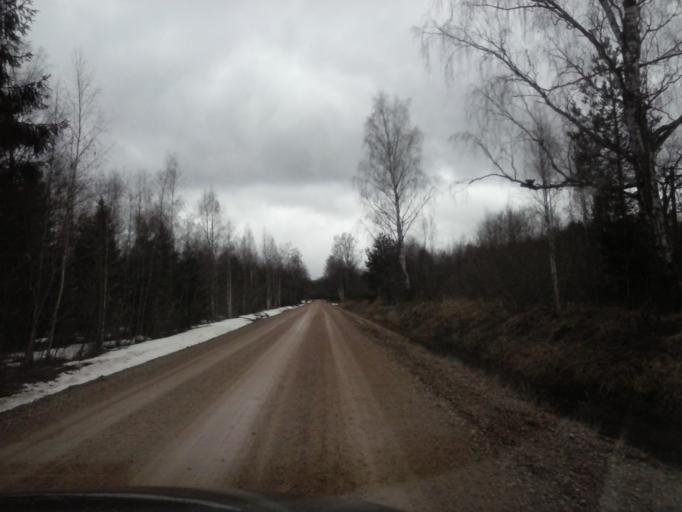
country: EE
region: Jogevamaa
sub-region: Mustvee linn
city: Mustvee
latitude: 59.0823
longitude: 26.8382
